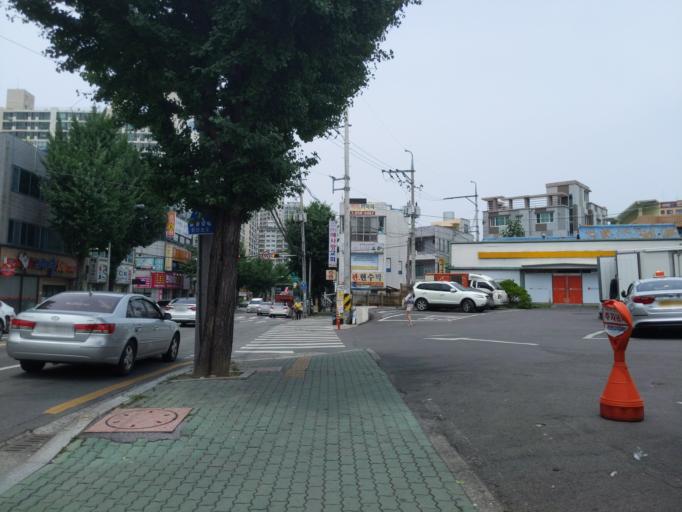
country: KR
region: Daegu
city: Hwawon
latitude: 35.8110
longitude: 128.5259
